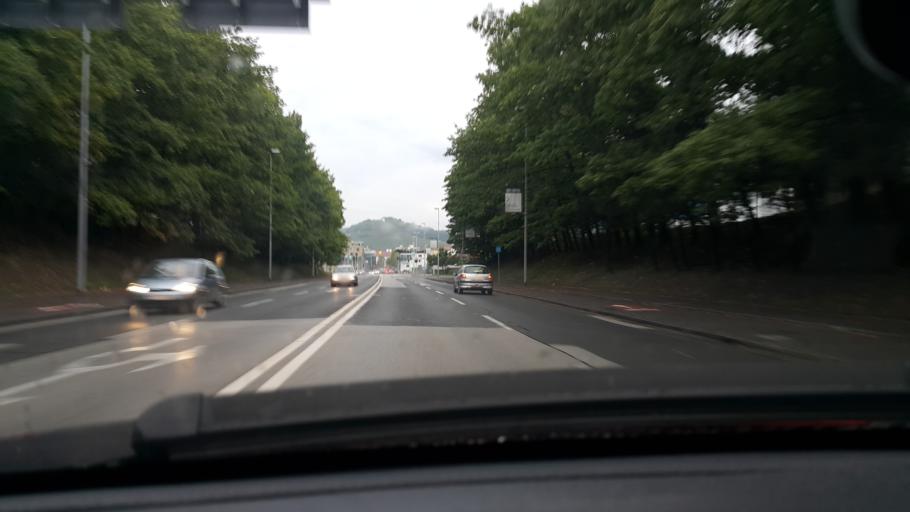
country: SI
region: Maribor
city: Maribor
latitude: 46.5525
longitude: 15.6503
